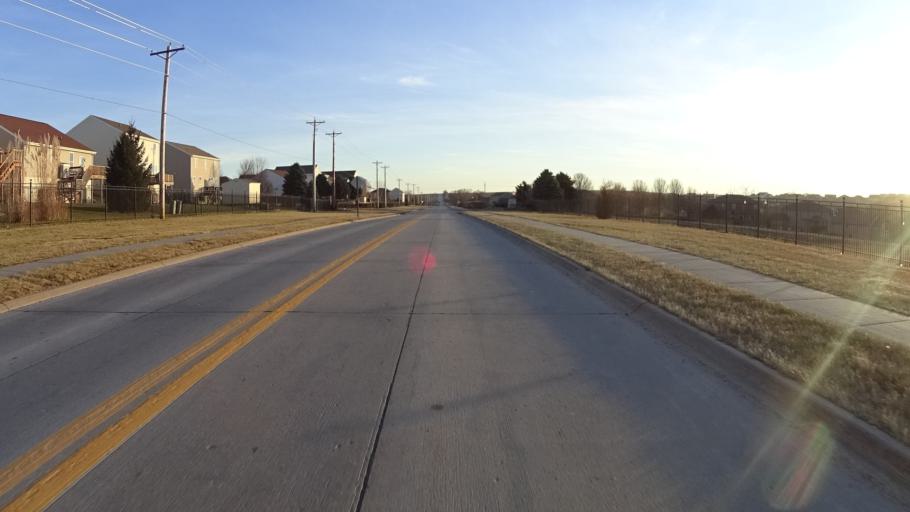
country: US
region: Nebraska
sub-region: Sarpy County
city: Papillion
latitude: 41.1316
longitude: -96.0621
